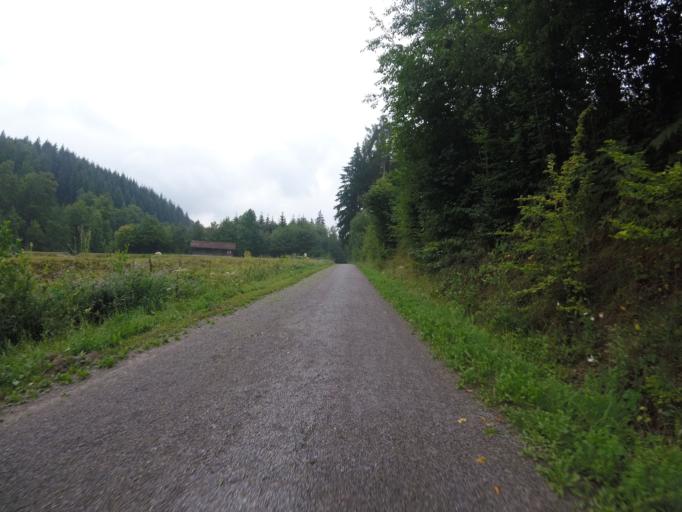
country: DE
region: Baden-Wuerttemberg
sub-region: Regierungsbezirk Stuttgart
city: Oppenweiler
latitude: 48.9865
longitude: 9.4303
